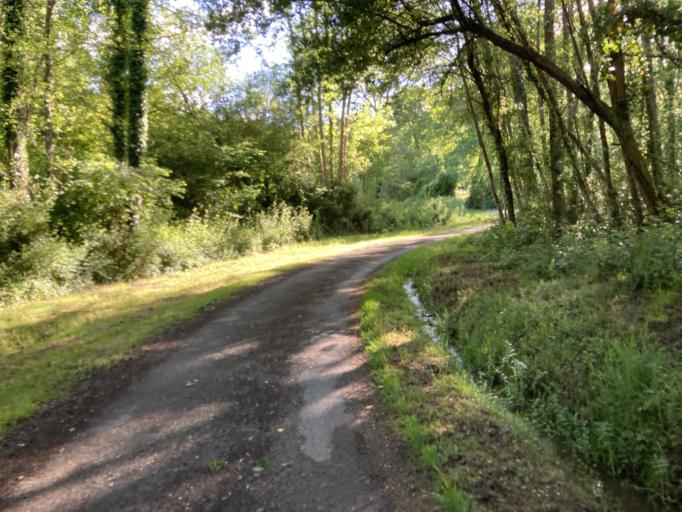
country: FR
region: Aquitaine
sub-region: Departement des Pyrenees-Atlantiques
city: Artiguelouve
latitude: 43.3164
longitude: -0.4797
